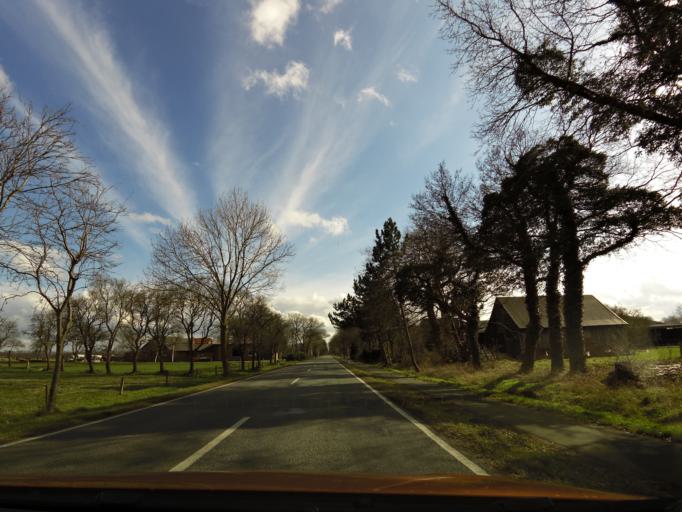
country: DE
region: Lower Saxony
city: Oldenburg
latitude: 53.0896
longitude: 8.2892
